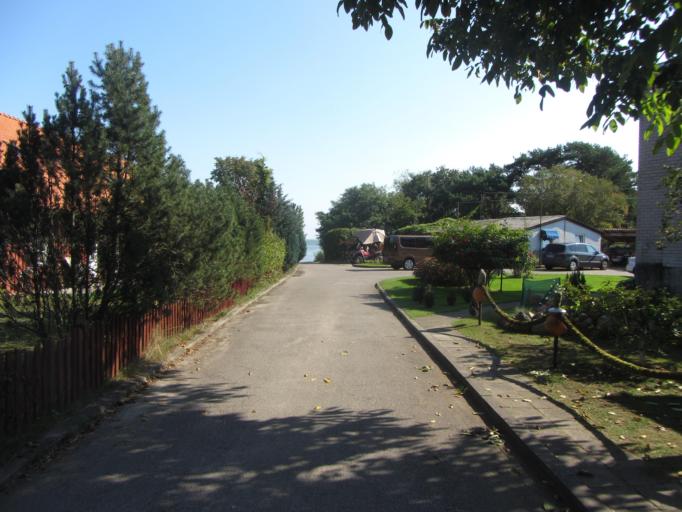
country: LT
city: Neringa
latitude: 55.3743
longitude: 21.0672
